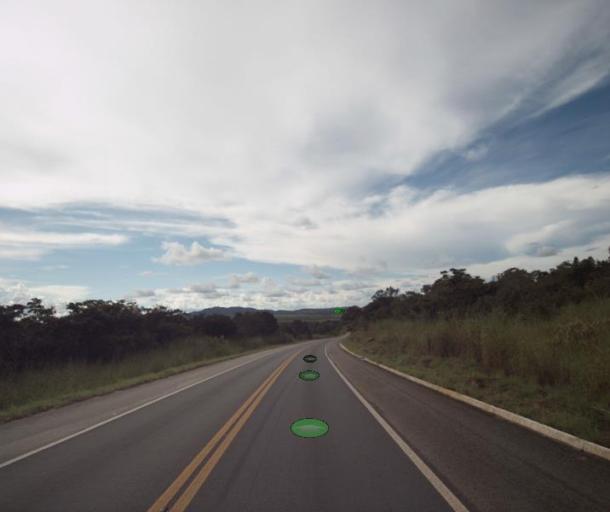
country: BR
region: Goias
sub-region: Barro Alto
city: Barro Alto
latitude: -15.1948
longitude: -48.7034
